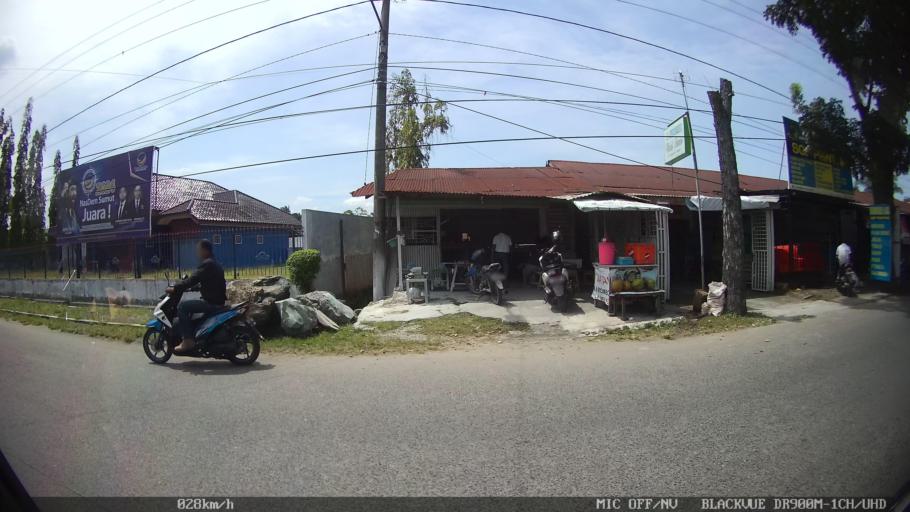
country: ID
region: North Sumatra
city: Sunggal
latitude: 3.5801
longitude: 98.6352
